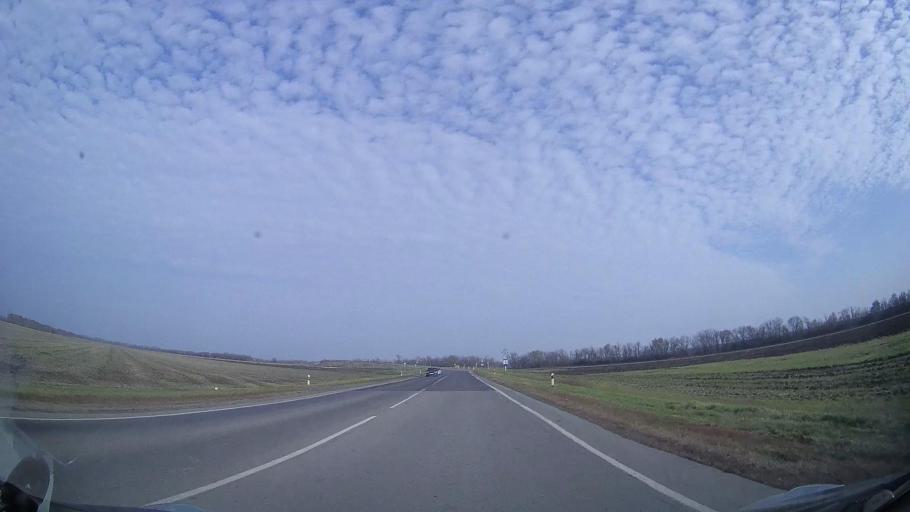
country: RU
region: Rostov
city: Tselina
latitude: 46.5238
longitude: 41.1628
